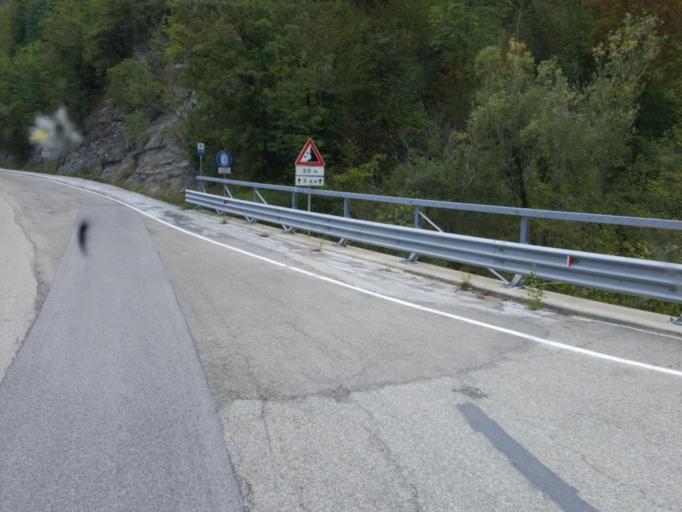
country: IT
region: Emilia-Romagna
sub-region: Forli-Cesena
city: San Piero in Bagno
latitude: 43.8237
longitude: 11.9575
